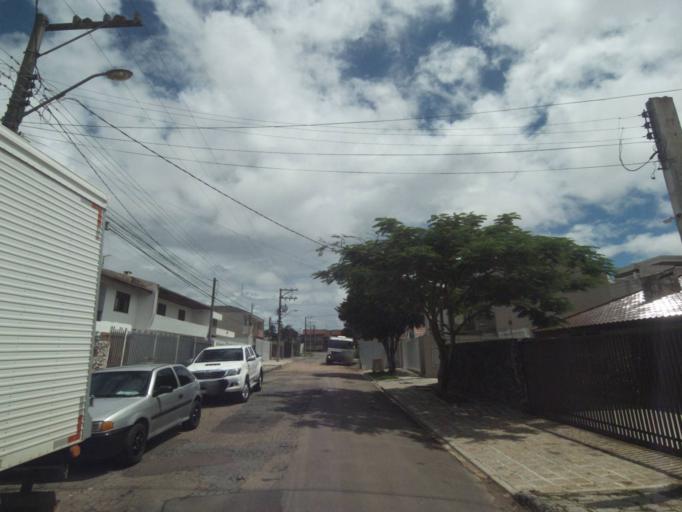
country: BR
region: Parana
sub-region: Curitiba
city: Curitiba
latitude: -25.4859
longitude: -49.2780
